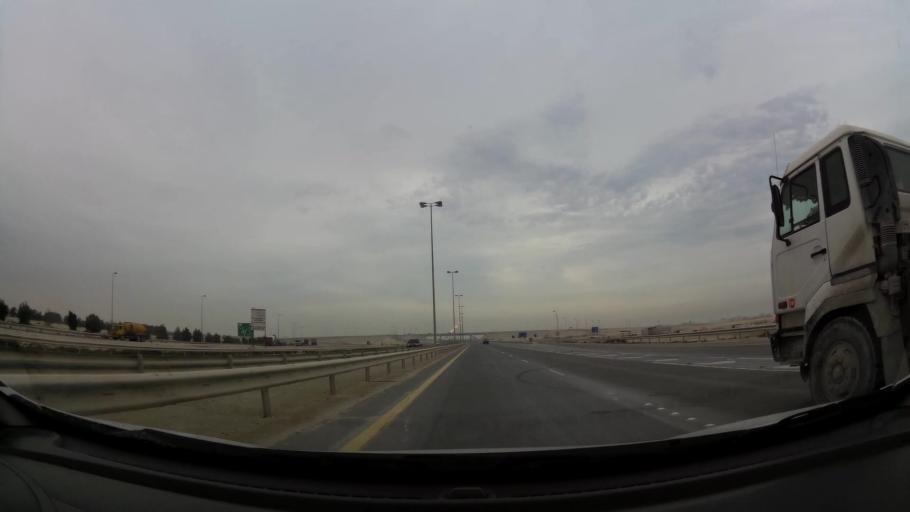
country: BH
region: Northern
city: Ar Rifa'
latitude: 26.0432
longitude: 50.6073
